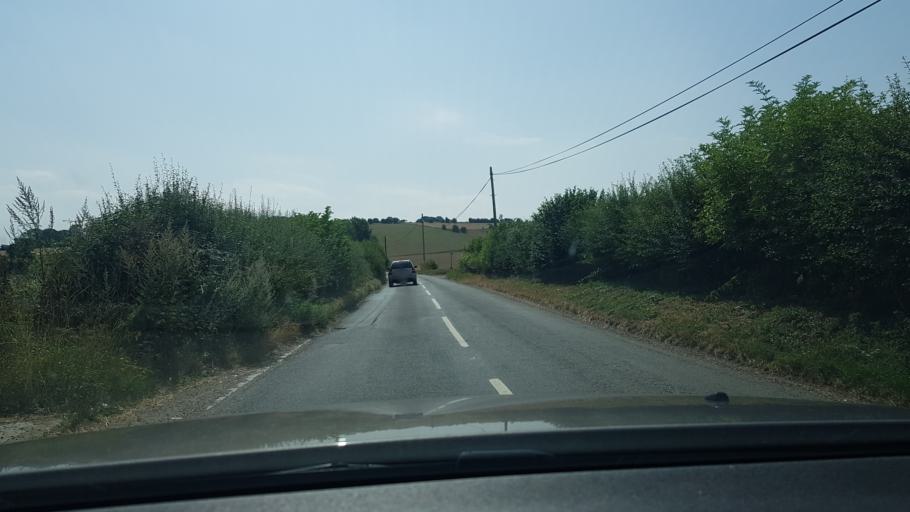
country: GB
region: England
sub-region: West Berkshire
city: Wickham
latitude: 51.4826
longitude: -1.4705
